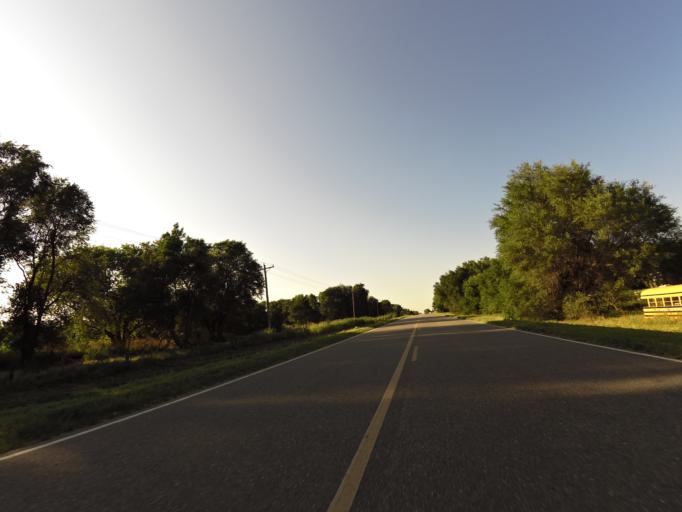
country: US
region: Kansas
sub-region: Reno County
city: Buhler
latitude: 38.1599
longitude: -97.8487
